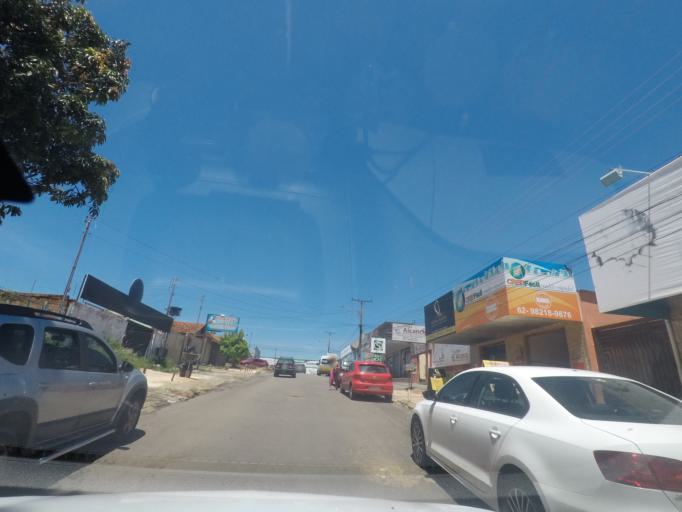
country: BR
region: Goias
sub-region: Aparecida De Goiania
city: Aparecida de Goiania
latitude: -16.7688
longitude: -49.3432
